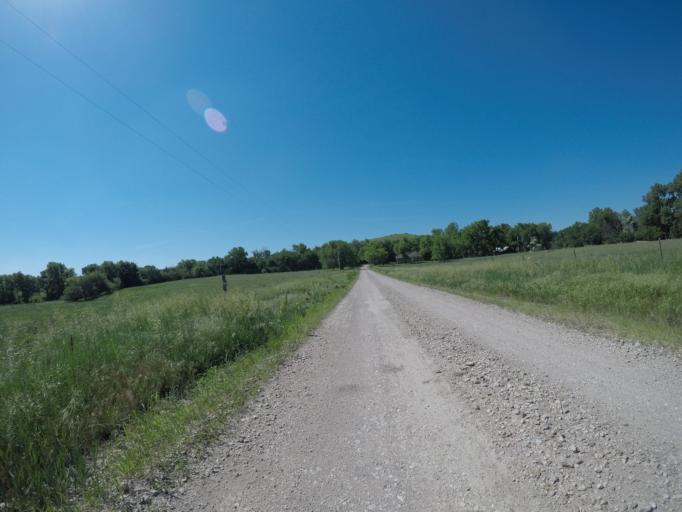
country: US
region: Kansas
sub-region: Wabaunsee County
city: Alma
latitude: 39.0212
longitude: -96.1506
